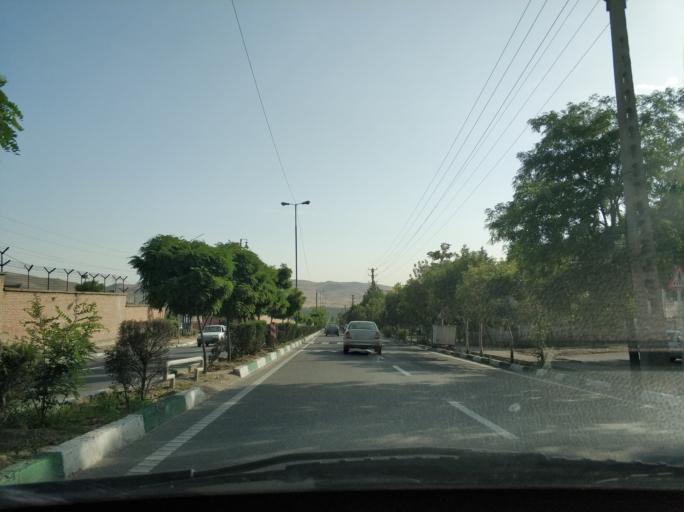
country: IR
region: Tehran
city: Tehran
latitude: 35.7287
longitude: 51.5916
